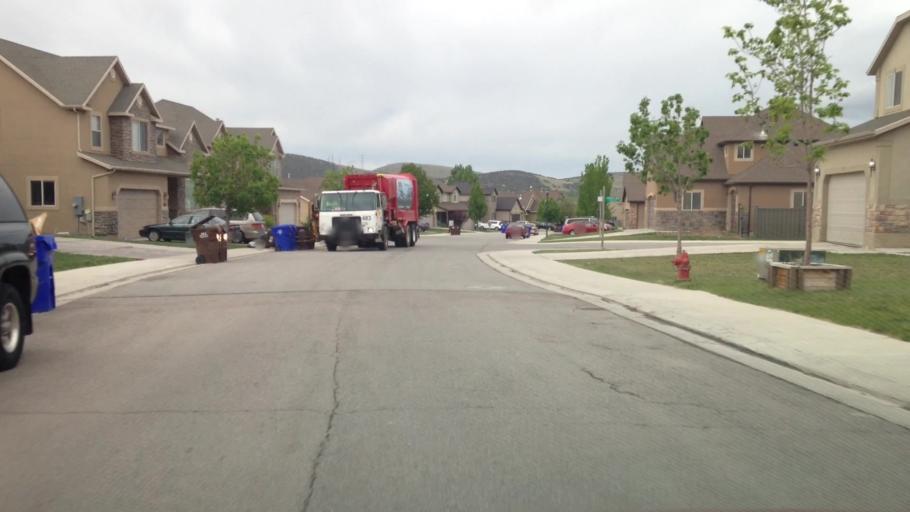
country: US
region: Utah
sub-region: Utah County
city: Saratoga Springs
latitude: 40.3745
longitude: -111.9694
